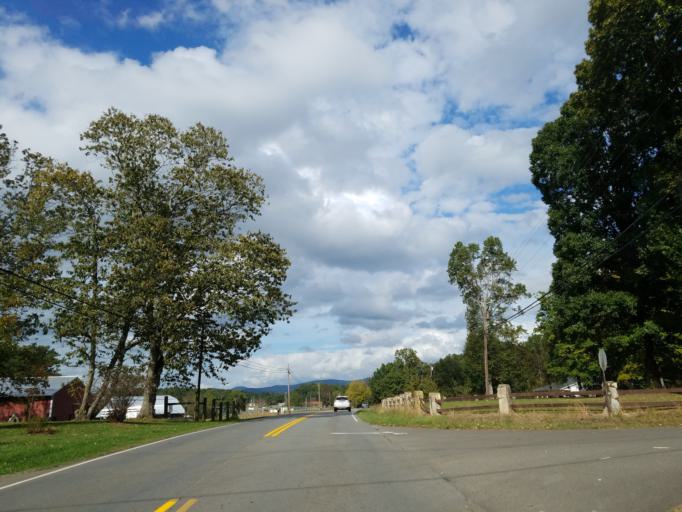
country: US
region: Georgia
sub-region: Pickens County
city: Jasper
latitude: 34.4395
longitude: -84.4223
